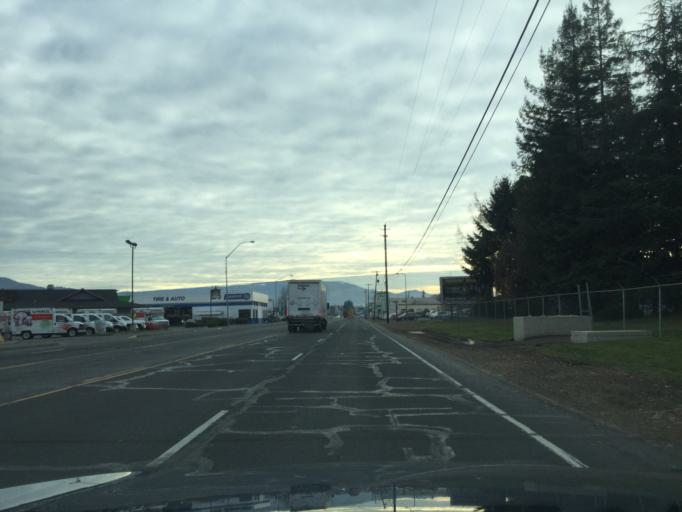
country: US
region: Oregon
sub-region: Jackson County
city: Medford
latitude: 42.3484
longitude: -122.8891
